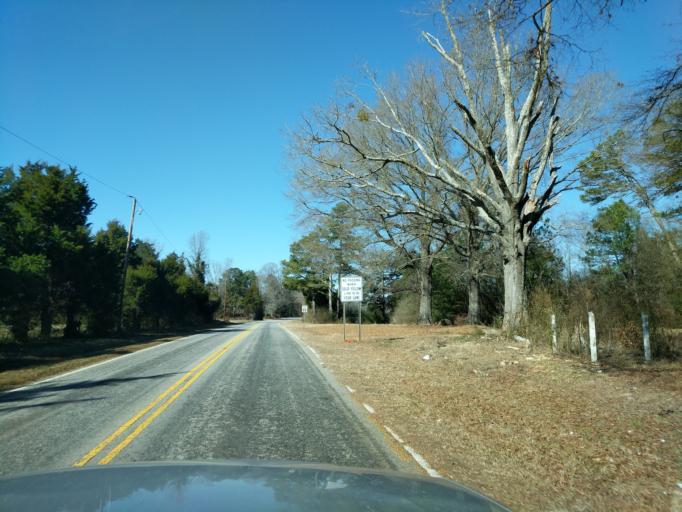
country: US
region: South Carolina
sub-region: Saluda County
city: Saluda
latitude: 34.0480
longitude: -81.8211
